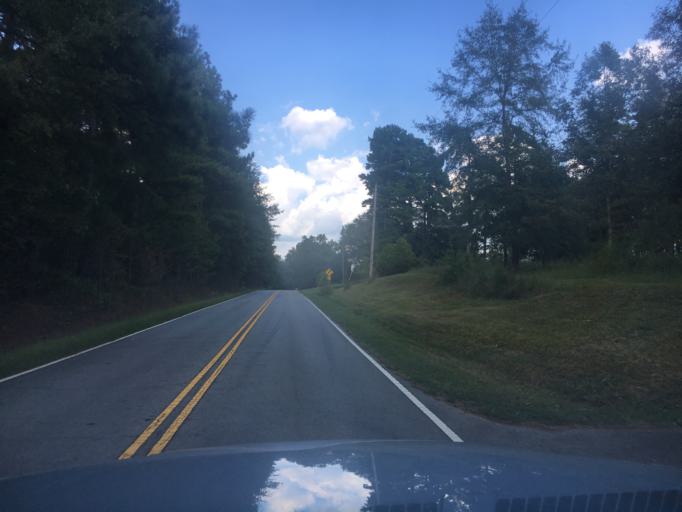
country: US
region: South Carolina
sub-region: Pickens County
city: Central
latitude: 34.7116
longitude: -82.7051
